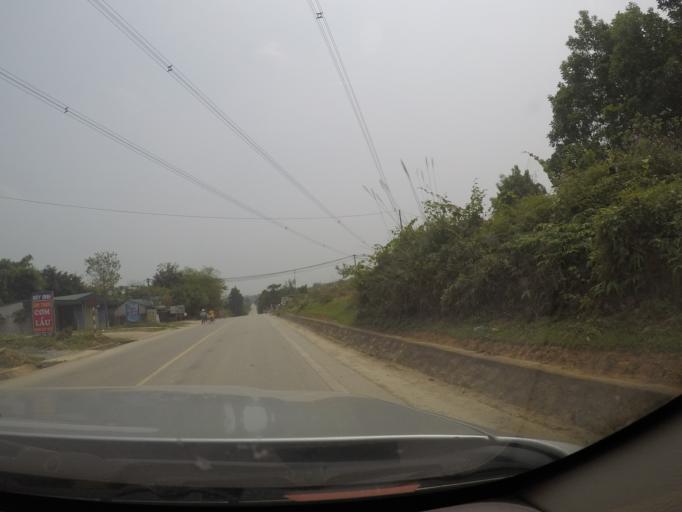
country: VN
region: Thanh Hoa
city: Thi Tran Yen Cat
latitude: 19.7146
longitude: 105.4341
